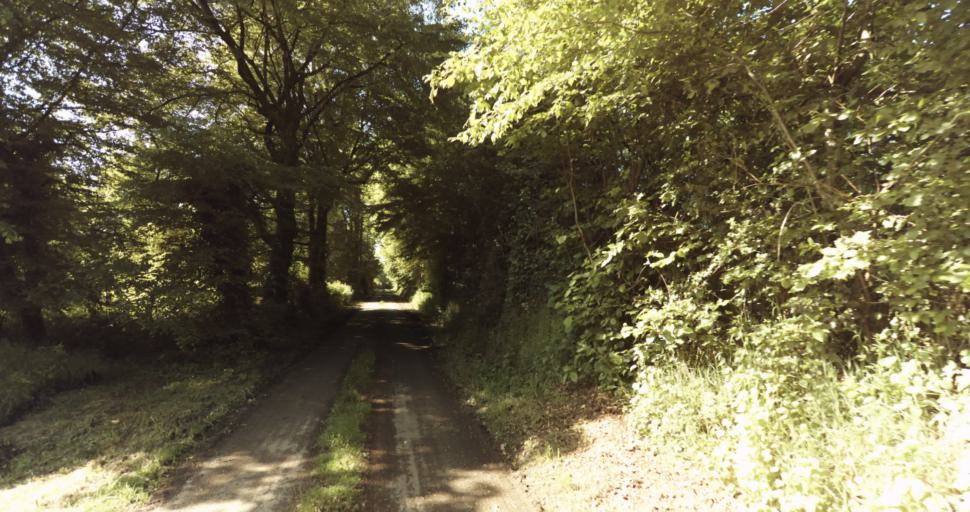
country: FR
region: Limousin
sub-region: Departement de la Haute-Vienne
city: Solignac
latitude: 45.7217
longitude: 1.2724
